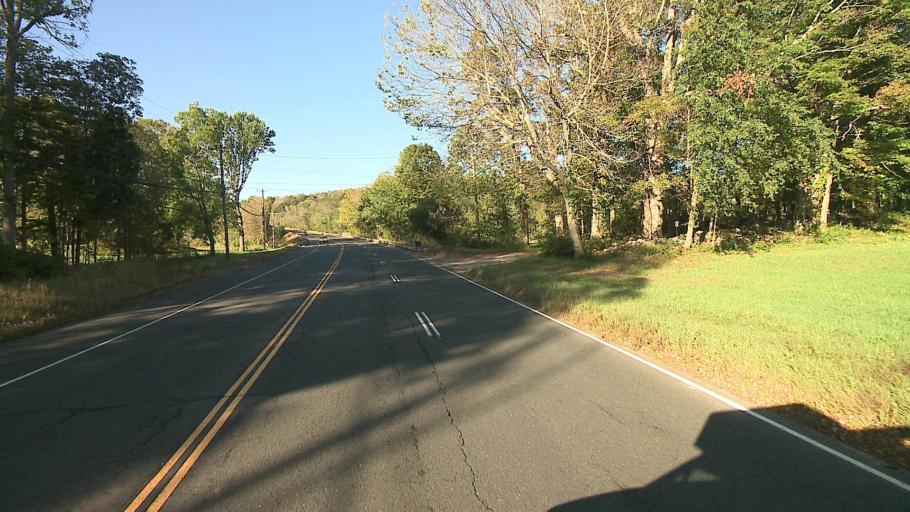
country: US
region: Connecticut
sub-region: Litchfield County
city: Northwest Harwinton
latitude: 41.8260
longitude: -73.0475
